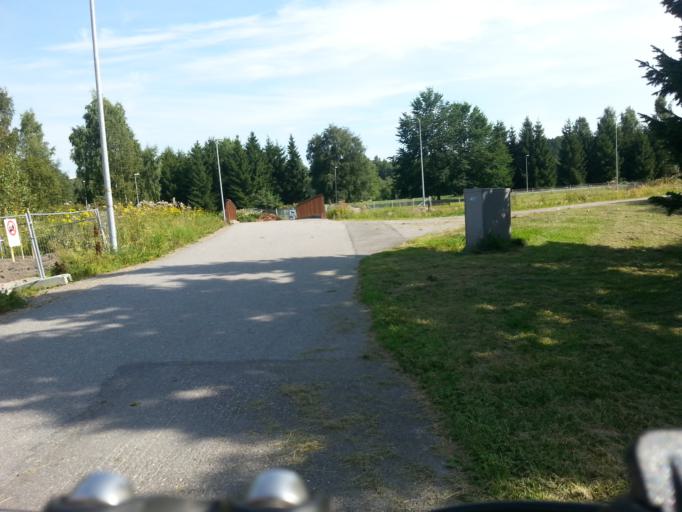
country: FI
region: Uusimaa
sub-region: Helsinki
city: Vantaa
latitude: 60.2394
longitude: 24.9936
